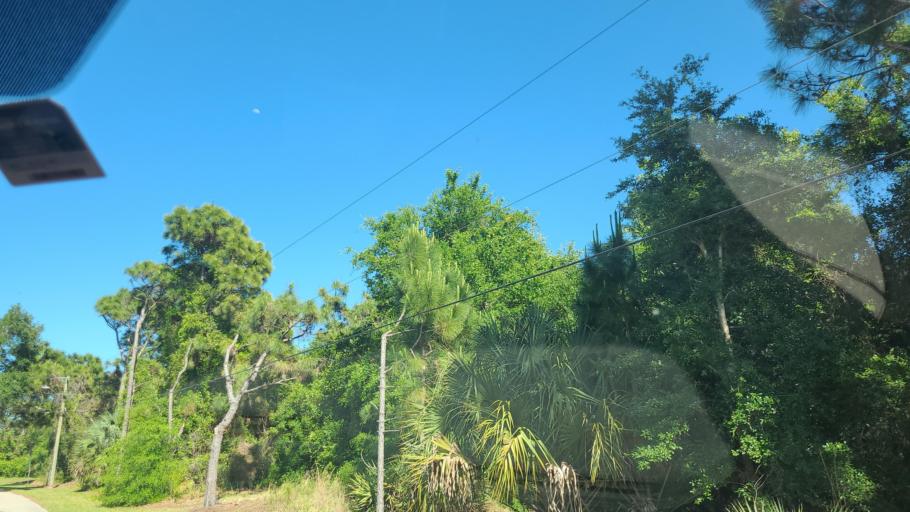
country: US
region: Florida
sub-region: Indian River County
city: Sebastian
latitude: 27.7667
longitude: -80.5019
